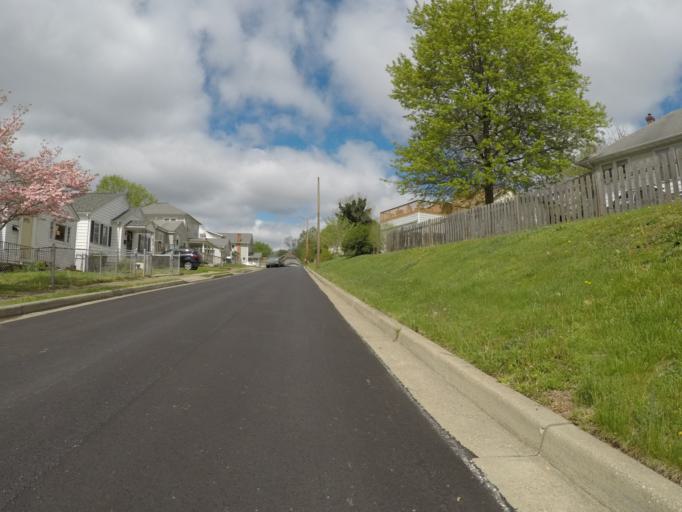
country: US
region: West Virginia
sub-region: Cabell County
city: Huntington
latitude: 38.4092
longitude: -82.4050
